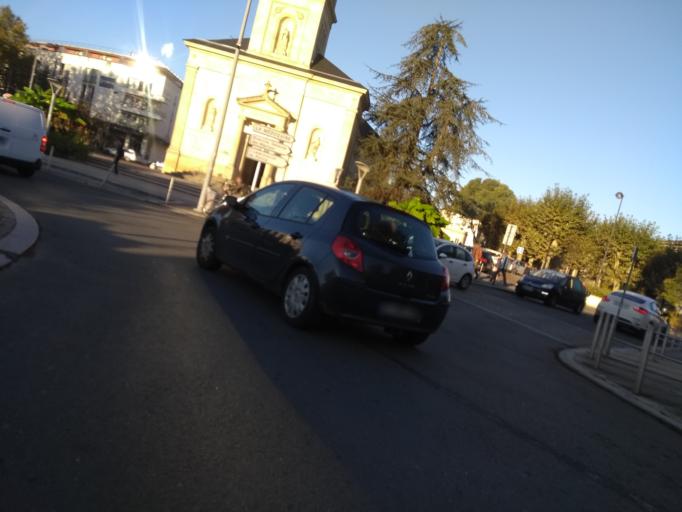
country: FR
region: Aquitaine
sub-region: Departement de la Gironde
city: Talence
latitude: 44.8128
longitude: -0.5908
